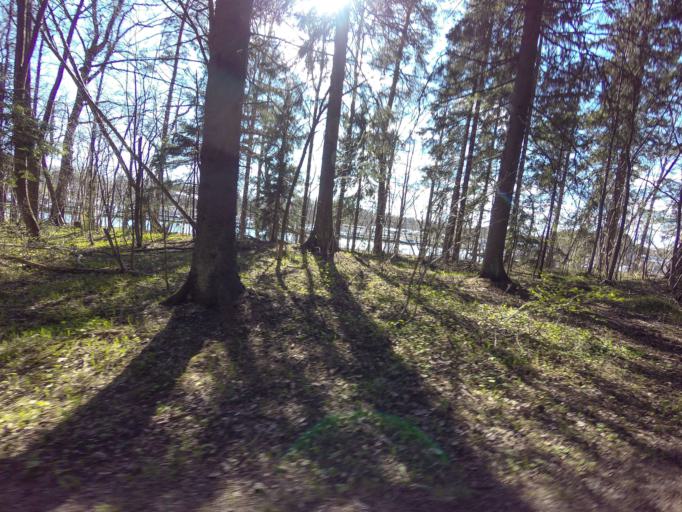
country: FI
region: Uusimaa
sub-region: Helsinki
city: Helsinki
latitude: 60.1674
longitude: 25.0618
